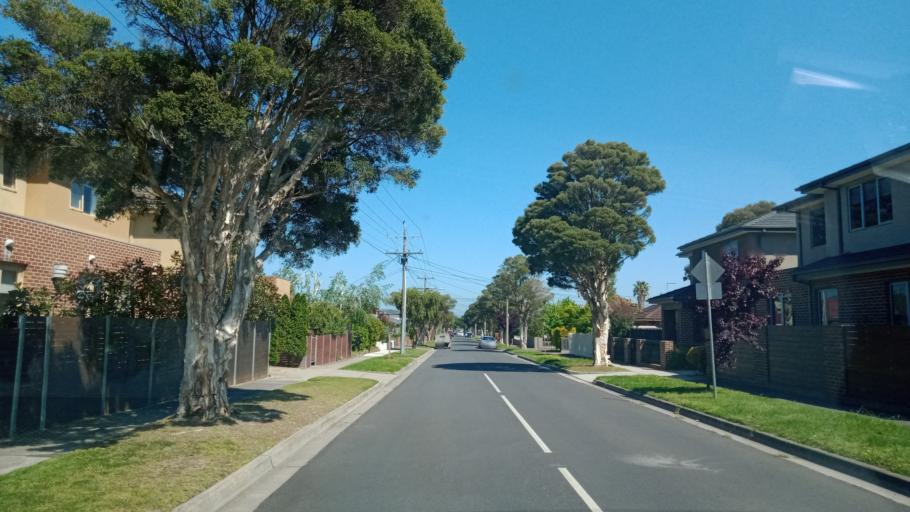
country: AU
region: Victoria
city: Murrumbeena
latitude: -37.9139
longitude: 145.0716
